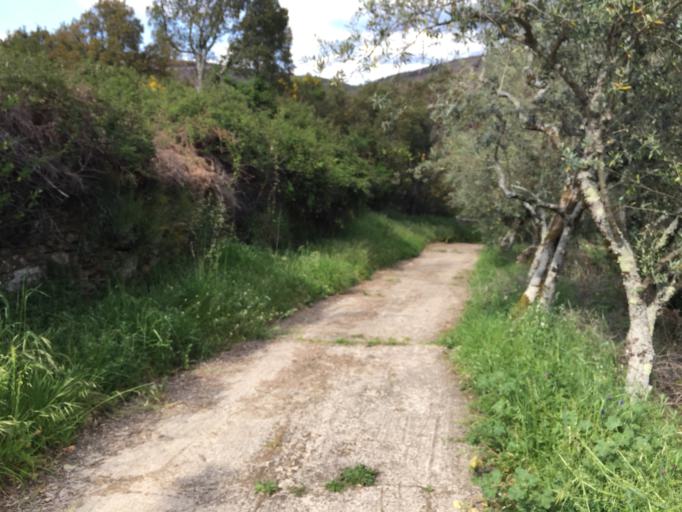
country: PT
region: Coimbra
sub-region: Pampilhosa da Serra
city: Pampilhosa da Serra
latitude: 40.1121
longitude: -7.8677
